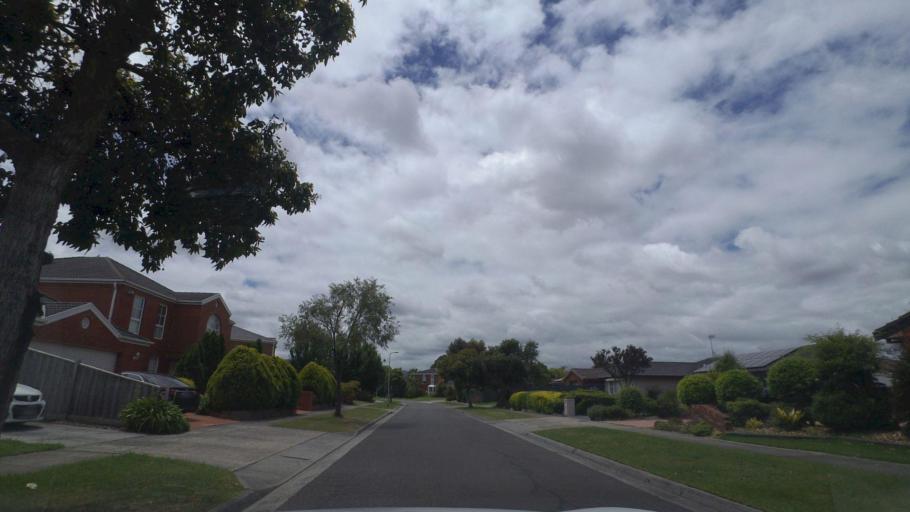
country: AU
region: Victoria
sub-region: Knox
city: Knoxfield
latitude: -37.9082
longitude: 145.2597
